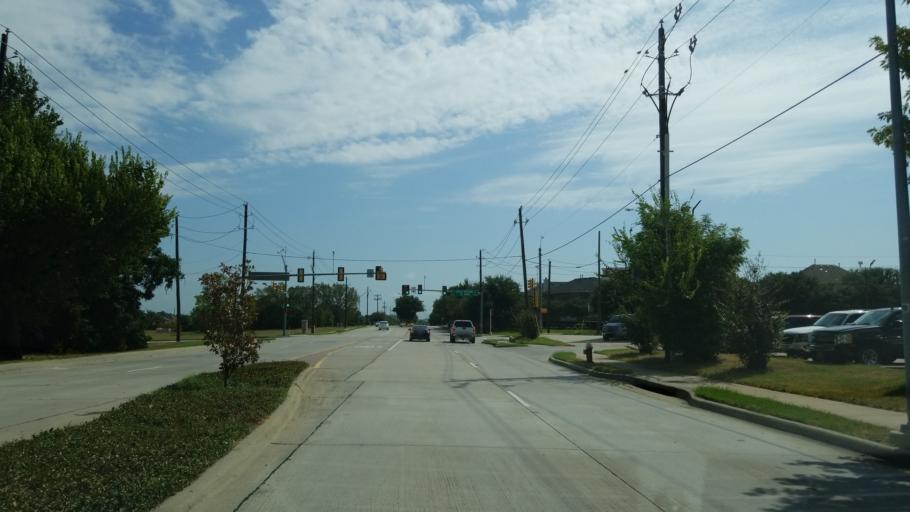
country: US
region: Texas
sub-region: Tarrant County
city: Euless
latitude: 32.8811
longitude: -97.0832
